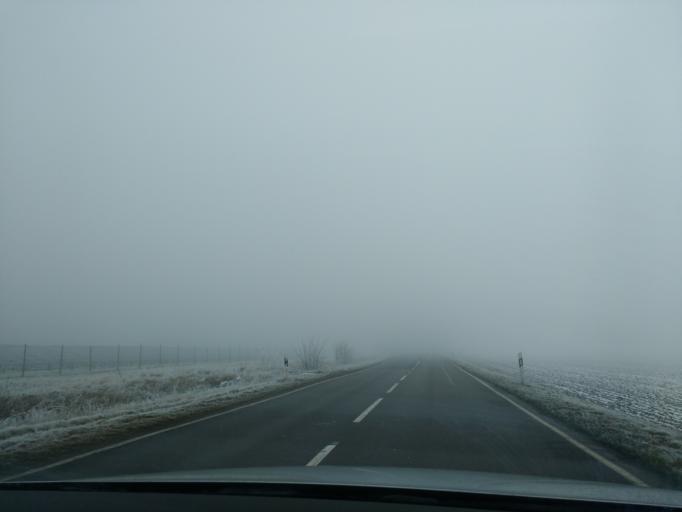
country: DE
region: Saxony-Anhalt
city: Oppin
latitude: 51.5488
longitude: 12.0471
